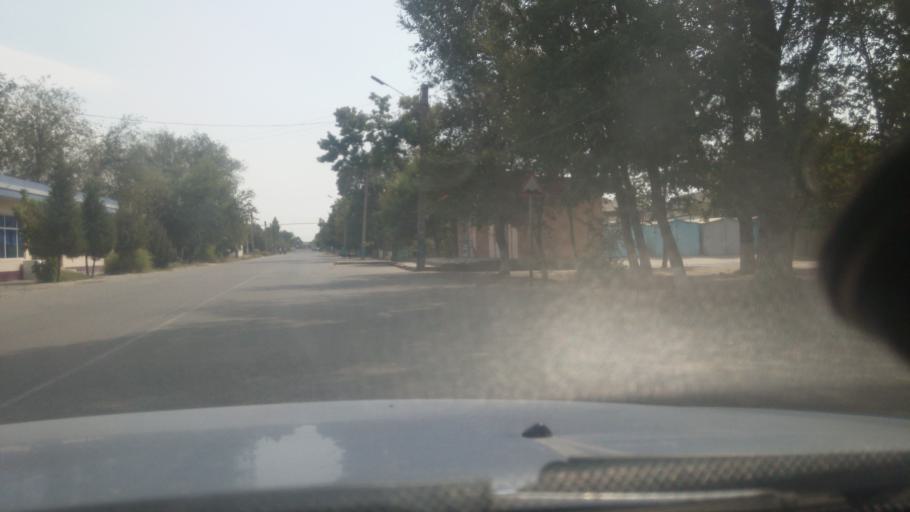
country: UZ
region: Sirdaryo
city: Guliston
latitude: 40.4964
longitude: 68.7823
